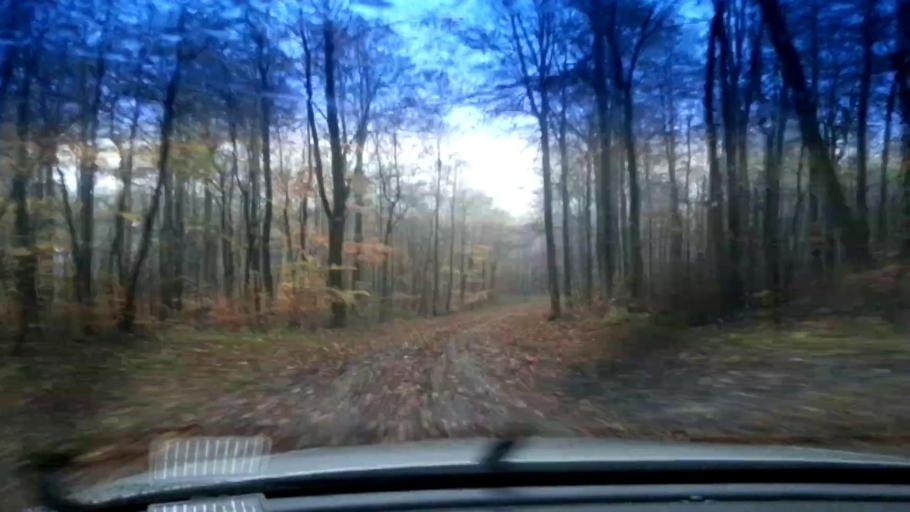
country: DE
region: Bavaria
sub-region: Upper Franconia
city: Schesslitz
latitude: 49.9379
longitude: 11.0585
